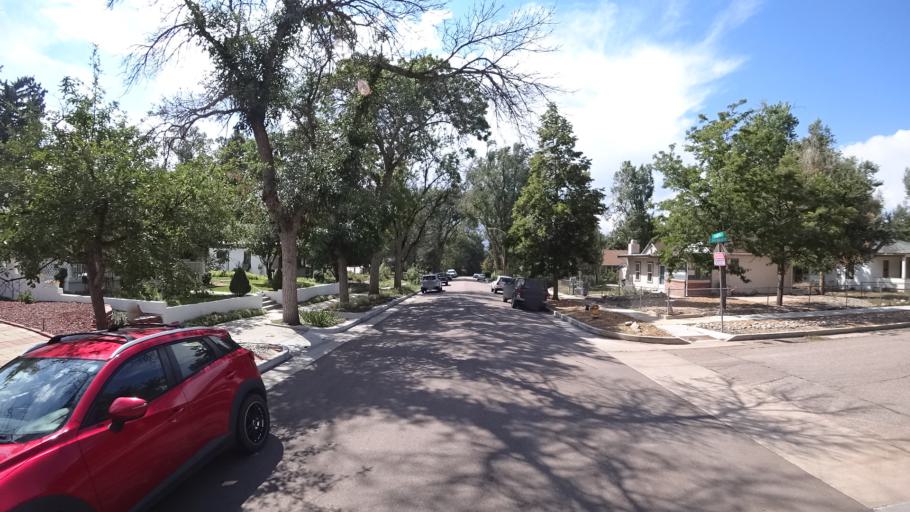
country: US
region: Colorado
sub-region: El Paso County
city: Colorado Springs
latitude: 38.8474
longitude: -104.8085
